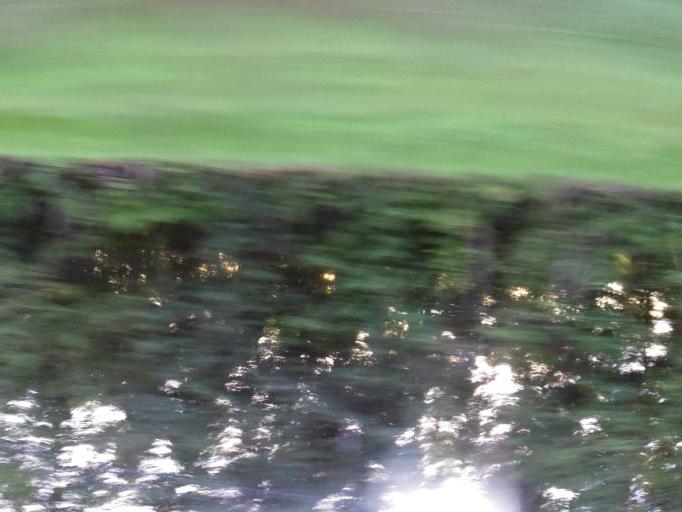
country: US
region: Georgia
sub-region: Camden County
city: Woodbine
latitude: 31.0149
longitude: -81.7315
